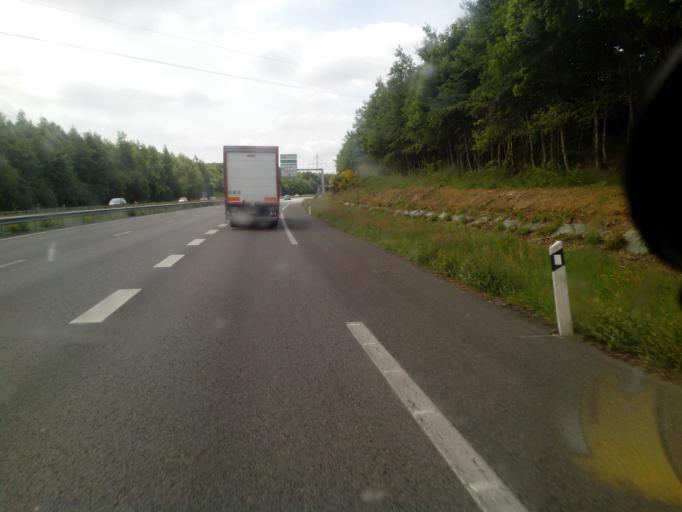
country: FR
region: Brittany
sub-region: Departement d'Ille-et-Vilaine
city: Cesson-Sevigne
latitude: 48.1431
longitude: -1.6216
